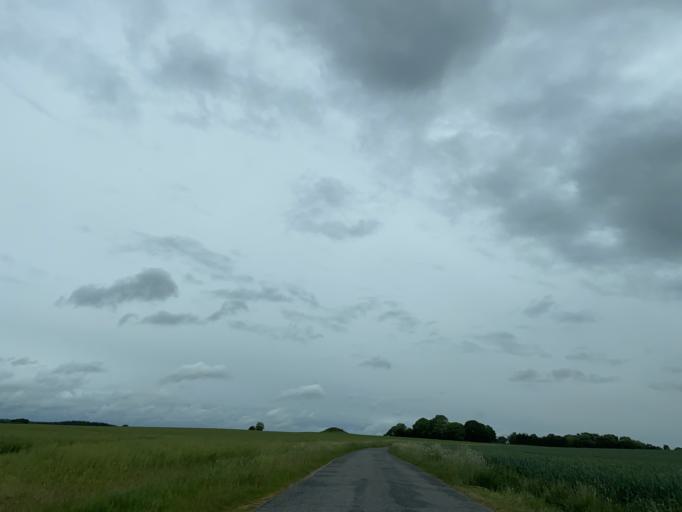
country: DK
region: Central Jutland
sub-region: Favrskov Kommune
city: Hammel
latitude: 56.2359
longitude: 9.7851
